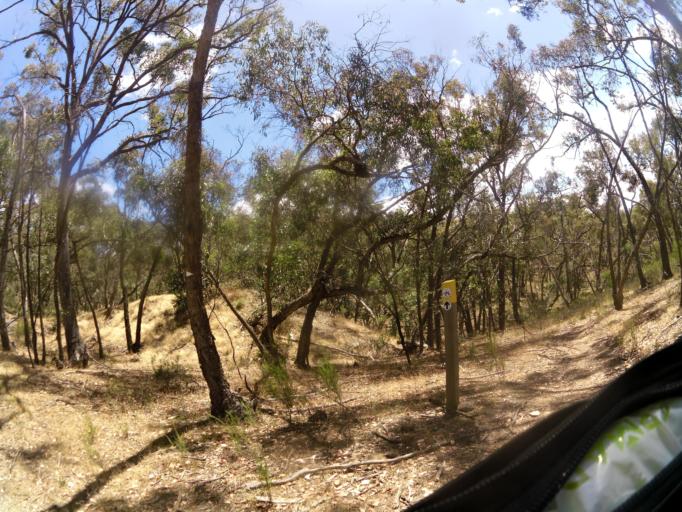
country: AU
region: Victoria
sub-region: Mount Alexander
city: Castlemaine
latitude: -37.0627
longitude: 144.2665
